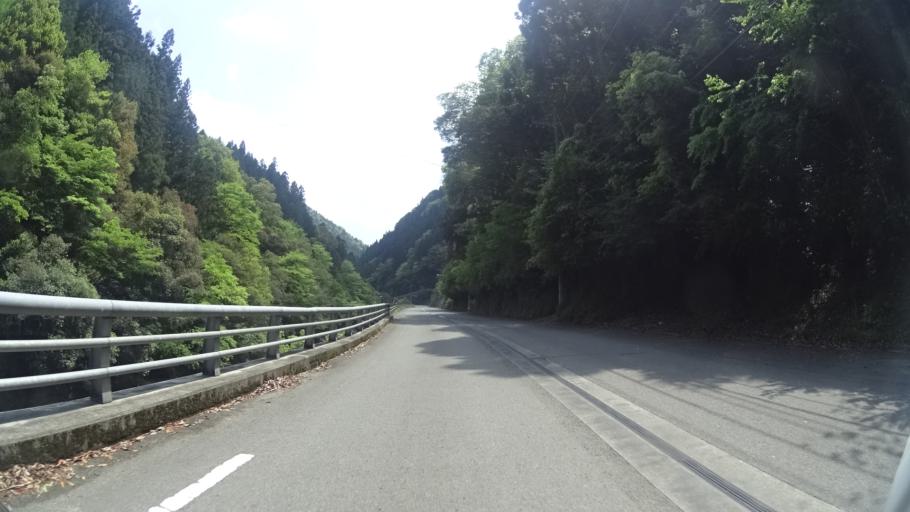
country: JP
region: Tokushima
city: Wakimachi
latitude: 33.9427
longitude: 134.0613
